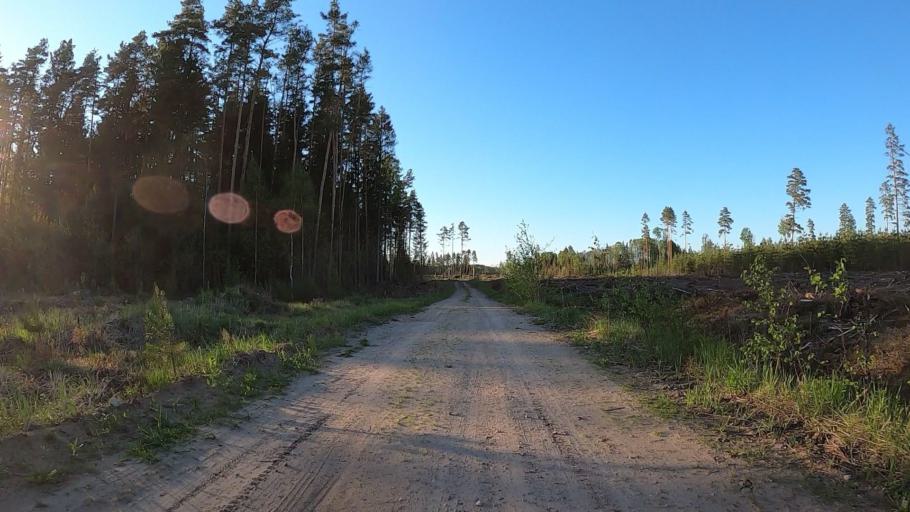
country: LV
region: Kekava
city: Kekava
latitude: 56.7727
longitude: 24.2226
